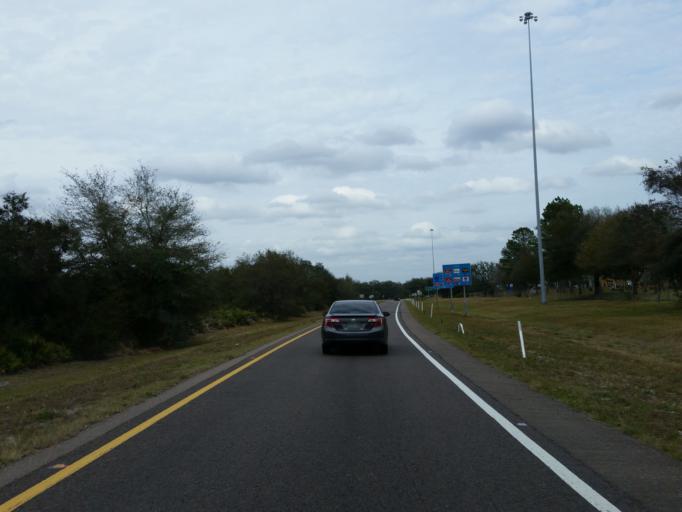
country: US
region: Florida
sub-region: Hillsborough County
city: Riverview
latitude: 27.8501
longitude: -82.3456
